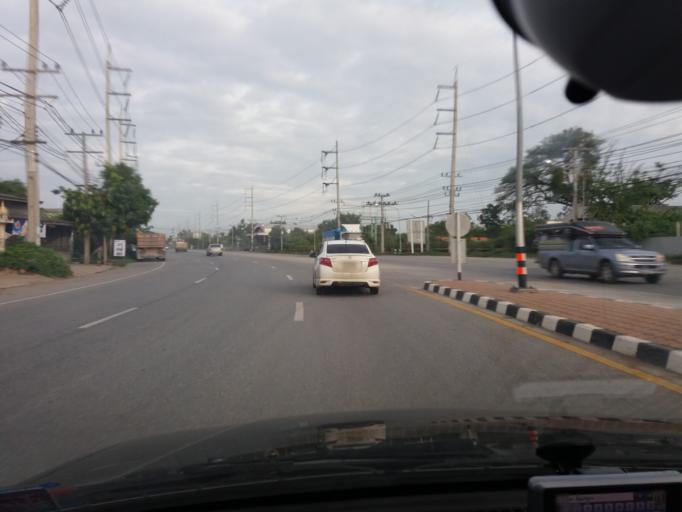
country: TH
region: Suphan Buri
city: U Thong
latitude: 14.3429
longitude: 99.8660
